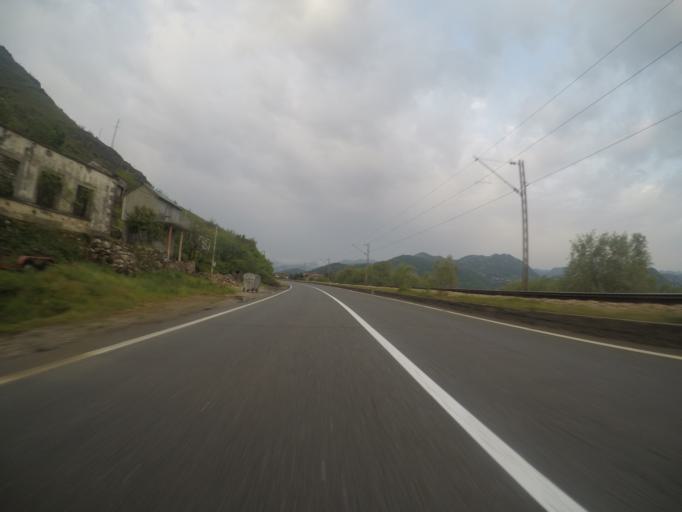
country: ME
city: Mojanovici
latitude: 42.2776
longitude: 19.1267
